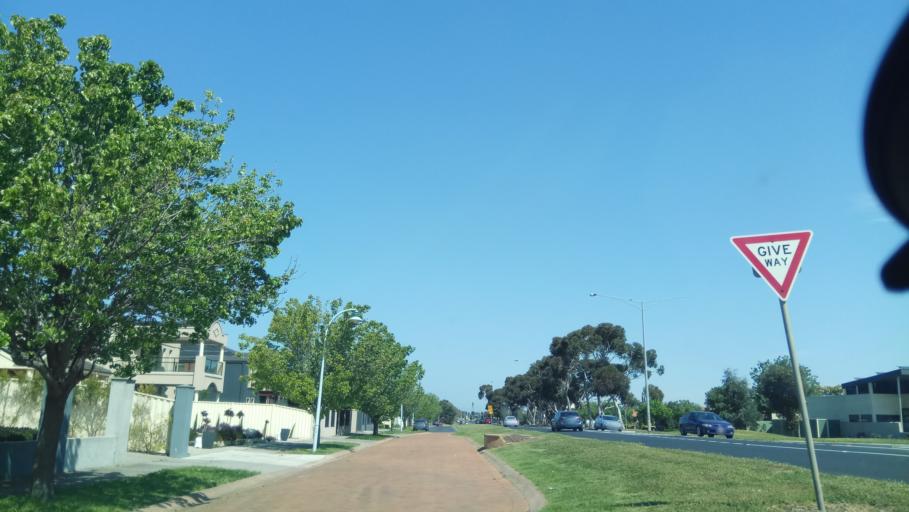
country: AU
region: Victoria
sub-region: Wyndham
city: Point Cook
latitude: -37.8894
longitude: 144.7557
